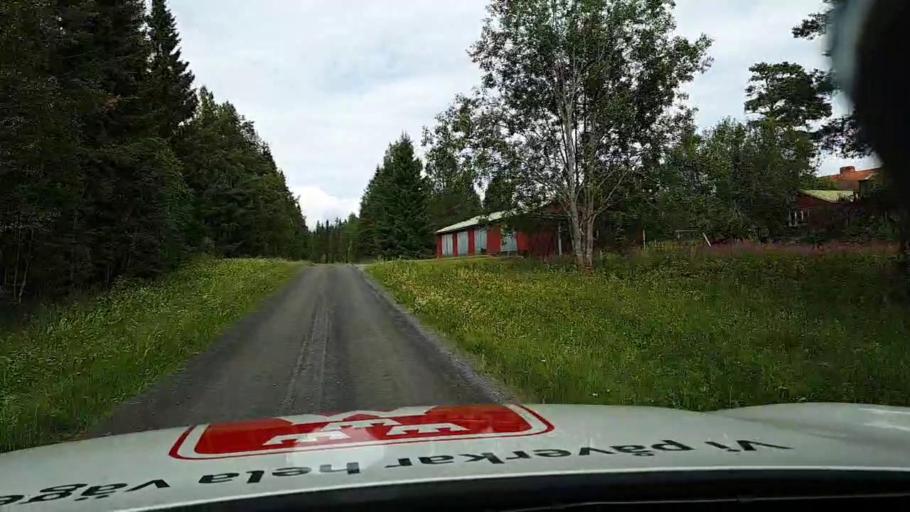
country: SE
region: Jaemtland
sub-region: OEstersunds Kommun
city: Lit
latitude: 63.2860
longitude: 15.2419
